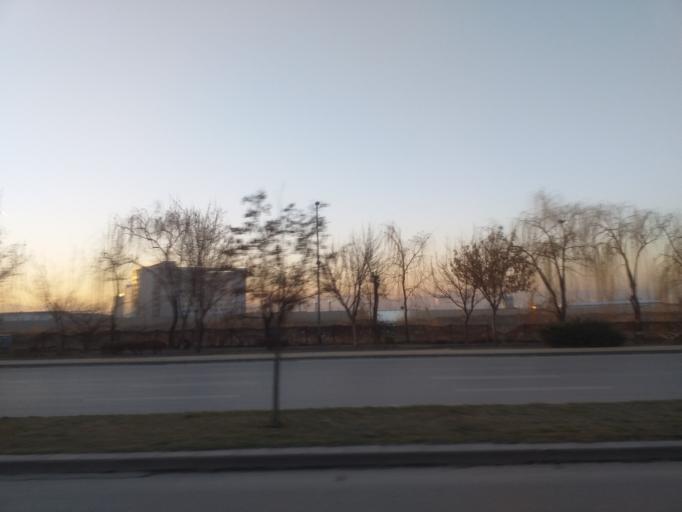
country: TR
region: Ankara
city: Ankara
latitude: 39.9689
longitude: 32.8268
